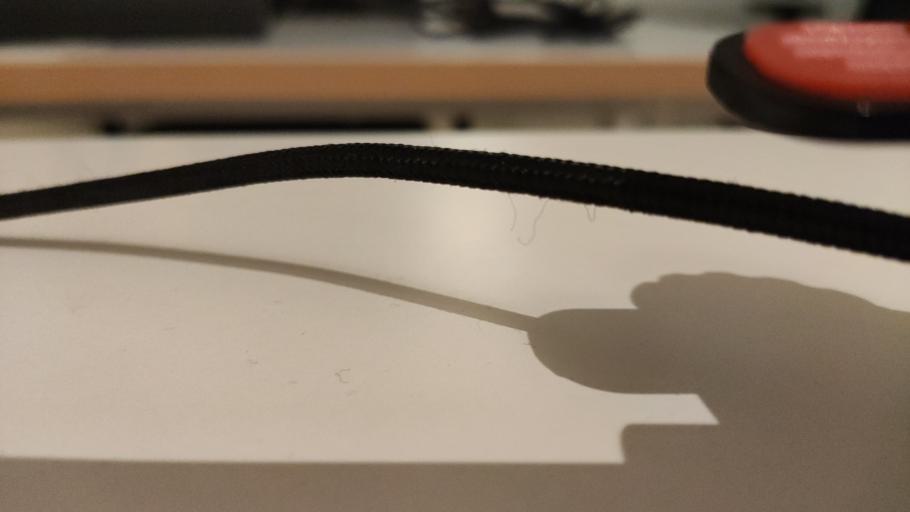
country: RU
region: Moskovskaya
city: Skoropuskovskiy
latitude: 56.3753
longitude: 38.1092
